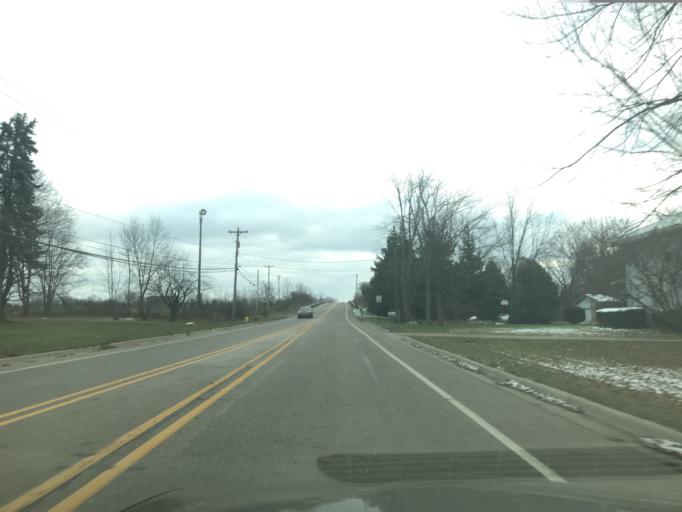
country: US
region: Michigan
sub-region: Eaton County
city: Waverly
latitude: 42.7265
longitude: -84.6730
